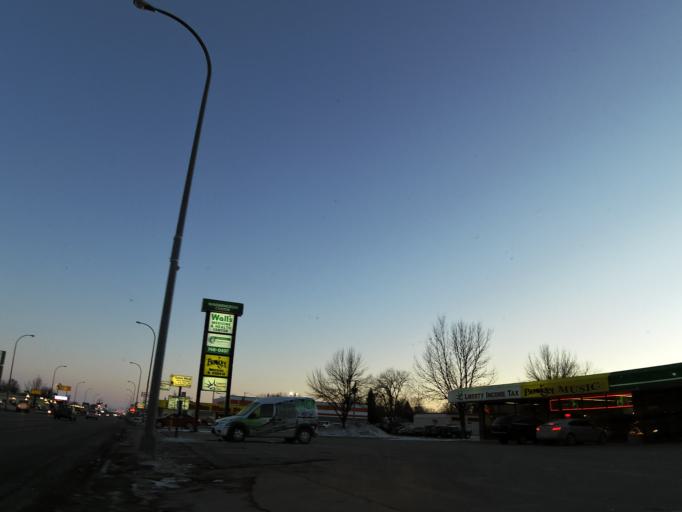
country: US
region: North Dakota
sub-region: Grand Forks County
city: Grand Forks
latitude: 47.9148
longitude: -97.0451
